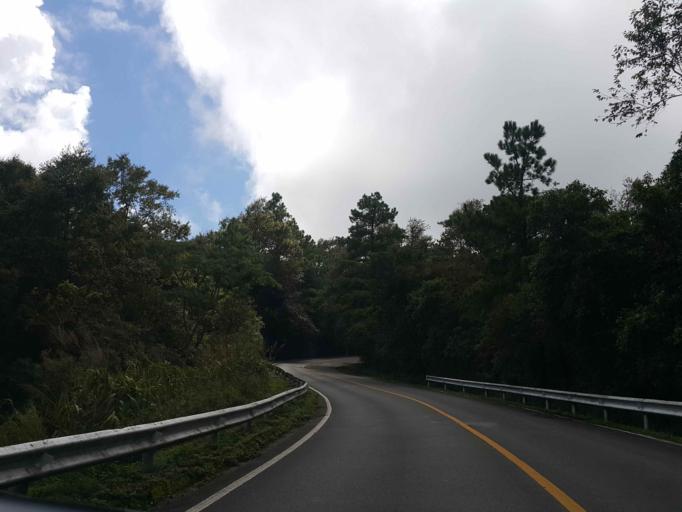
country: TH
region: Chiang Mai
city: Mae Chaem
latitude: 18.5373
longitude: 98.4922
